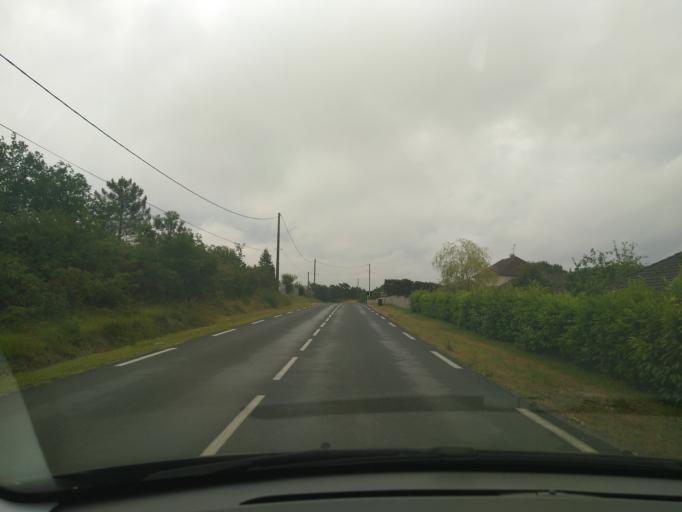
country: FR
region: Limousin
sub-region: Departement de la Correze
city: Brive-la-Gaillarde
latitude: 45.1047
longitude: 1.5486
